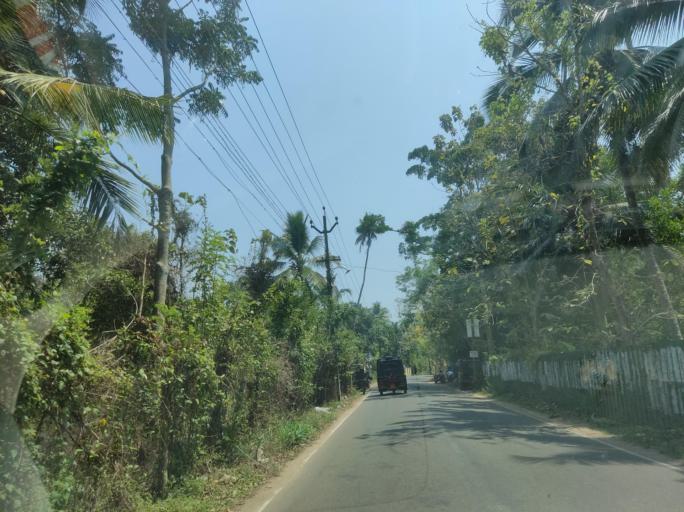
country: IN
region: Kerala
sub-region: Alappuzha
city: Kutiatodu
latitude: 9.8158
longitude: 76.2995
